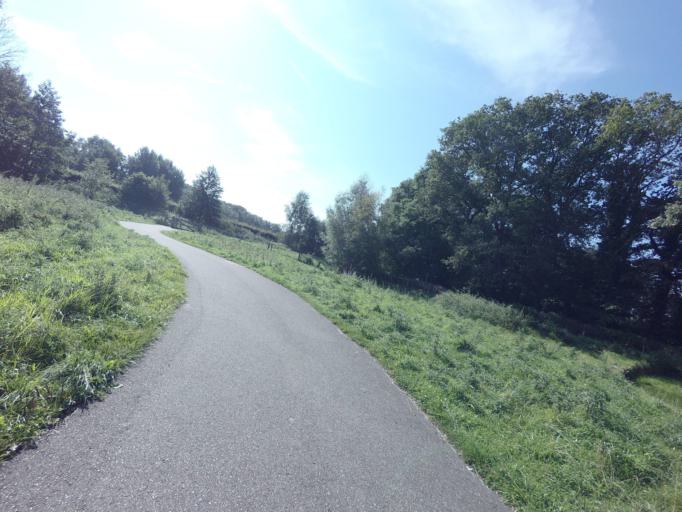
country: NL
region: Overijssel
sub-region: Gemeente Enschede
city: Enschede
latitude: 52.1868
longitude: 6.8496
